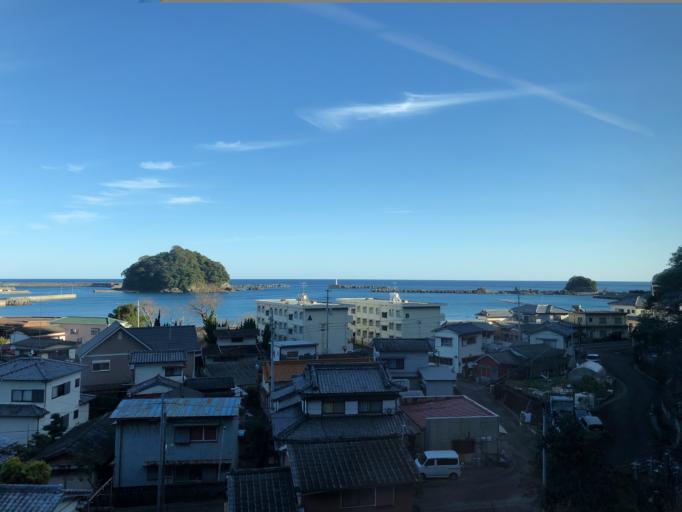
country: JP
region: Kochi
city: Nakamura
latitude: 33.0753
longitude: 133.1042
